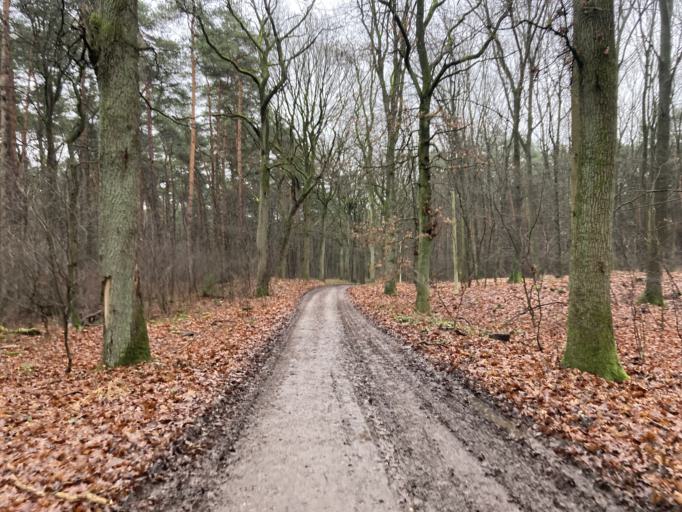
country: DE
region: North Rhine-Westphalia
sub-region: Regierungsbezirk Dusseldorf
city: Niederkruchten
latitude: 51.1749
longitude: 6.1989
